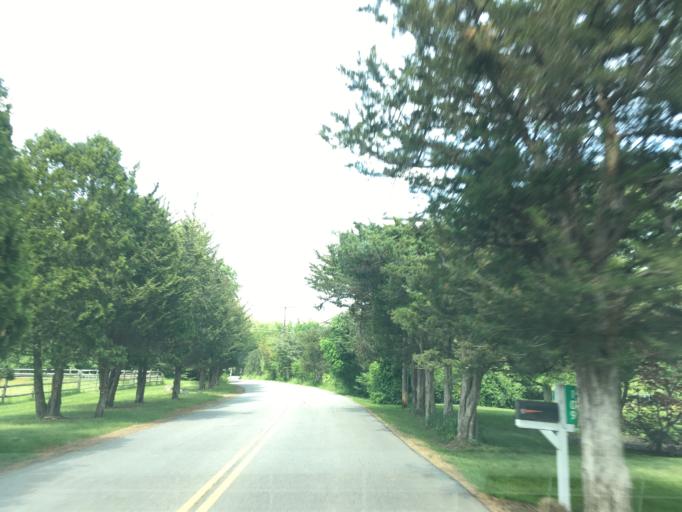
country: US
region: New Hampshire
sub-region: Rockingham County
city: Stratham Station
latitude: 43.0271
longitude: -70.8703
